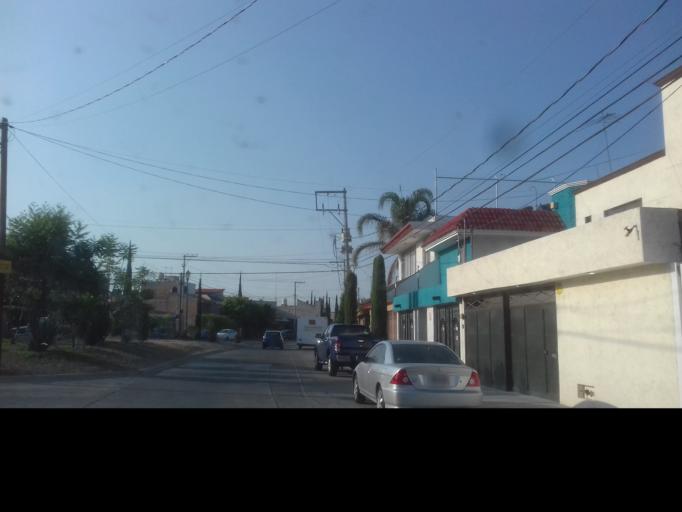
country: MX
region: Aguascalientes
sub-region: Aguascalientes
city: Aguascalientes
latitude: 21.8537
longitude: -102.2847
